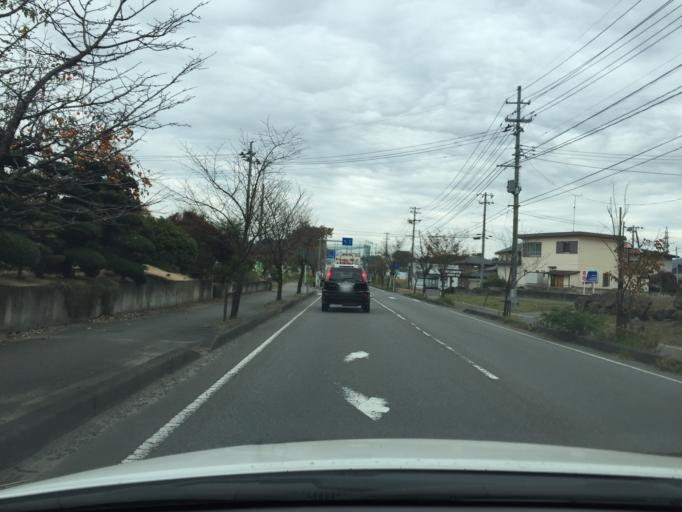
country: JP
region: Tochigi
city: Kuroiso
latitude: 37.1065
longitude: 140.2187
